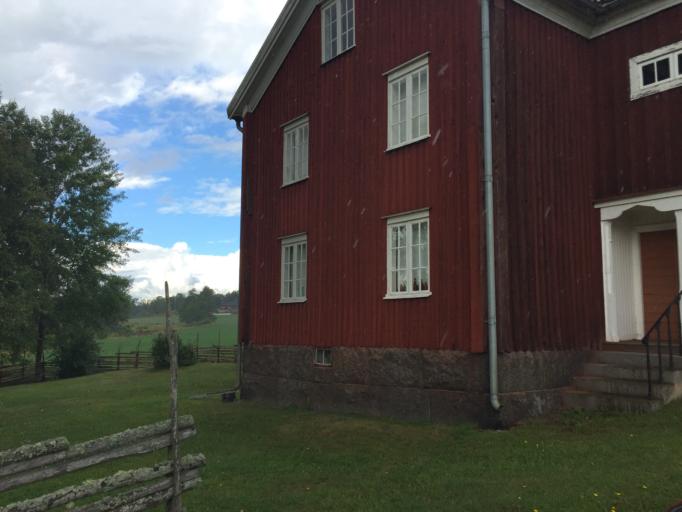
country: SE
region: Kalmar
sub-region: Vasterviks Kommun
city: Gamleby
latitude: 57.8018
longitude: 16.4636
